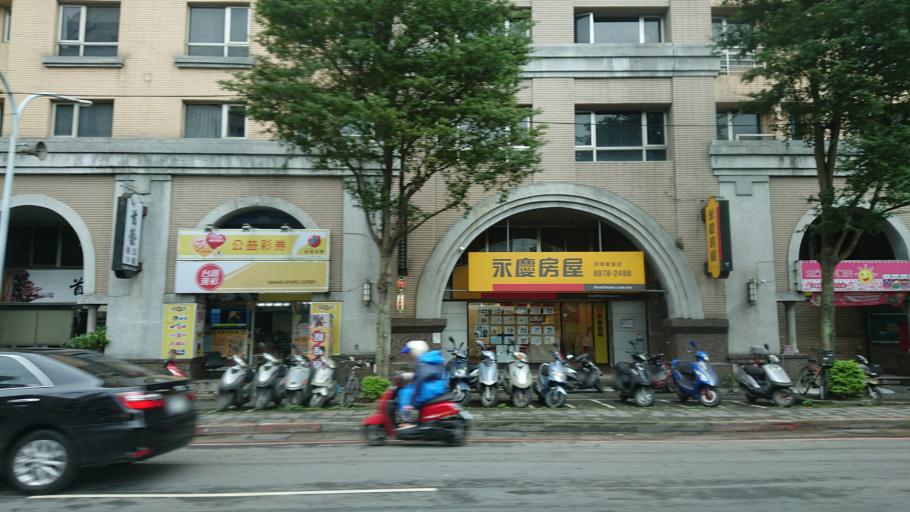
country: TW
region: Taipei
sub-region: Taipei
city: Banqiao
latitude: 24.9536
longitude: 121.4122
